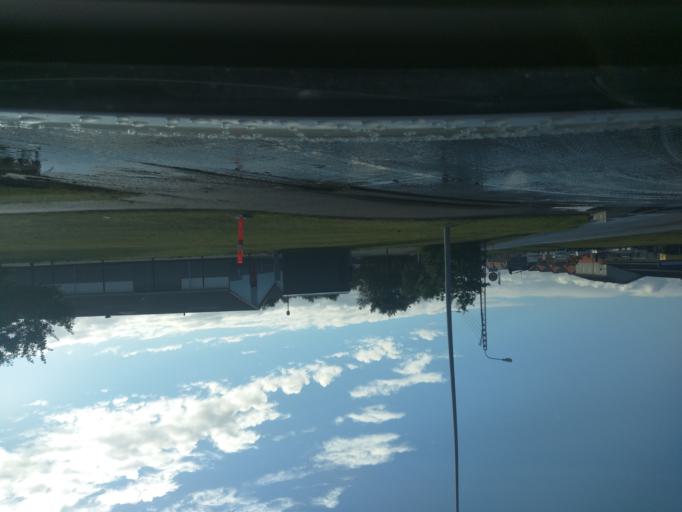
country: DK
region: Central Jutland
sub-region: Viborg Kommune
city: Viborg
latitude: 56.4727
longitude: 9.4042
